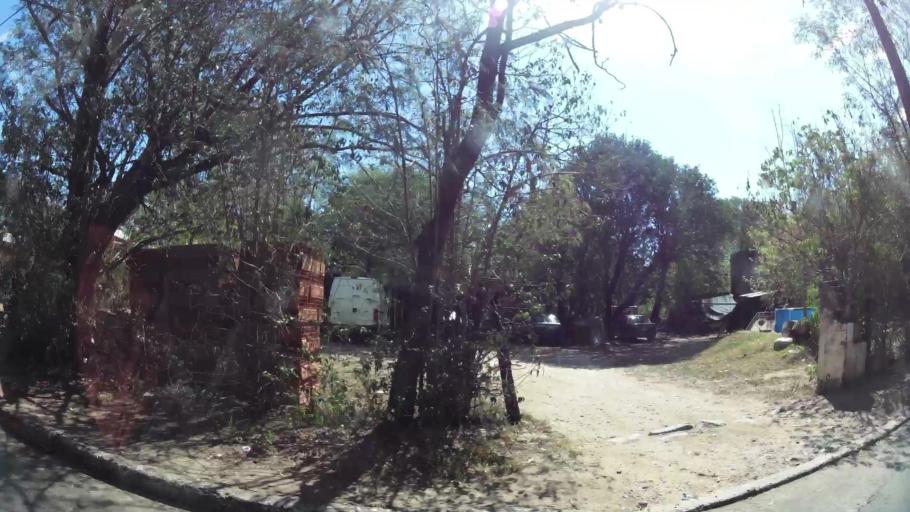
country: AR
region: Cordoba
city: Saldan
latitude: -31.2988
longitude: -64.3015
